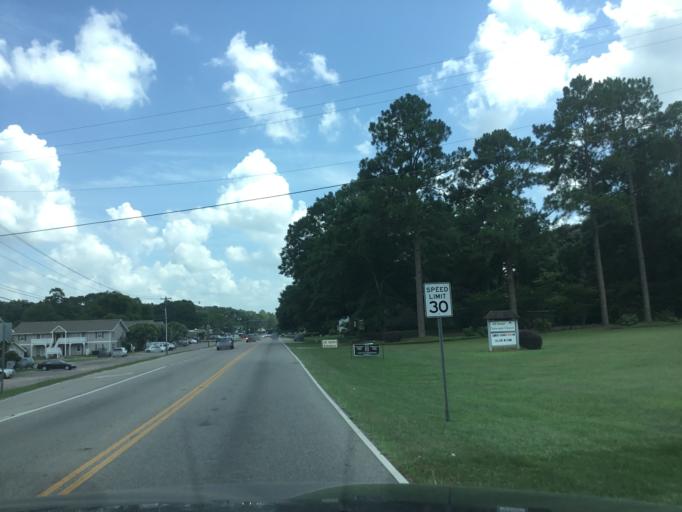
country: US
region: Alabama
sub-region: Montgomery County
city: Montgomery
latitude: 32.3961
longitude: -86.2594
